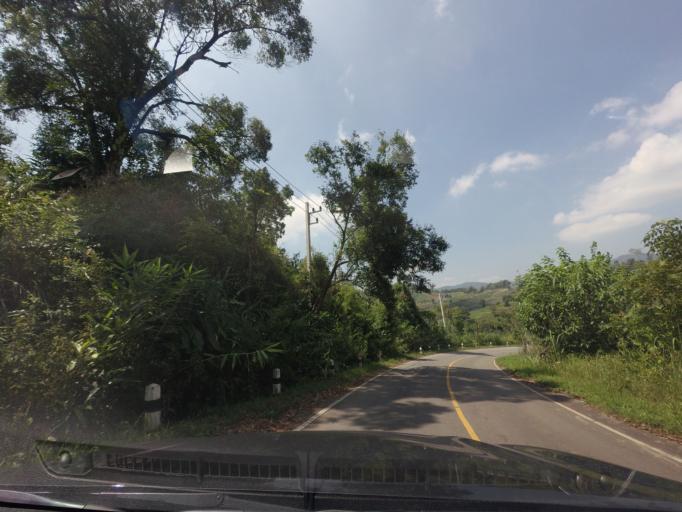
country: TH
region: Loei
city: Na Haeo
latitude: 17.4919
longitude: 100.8928
